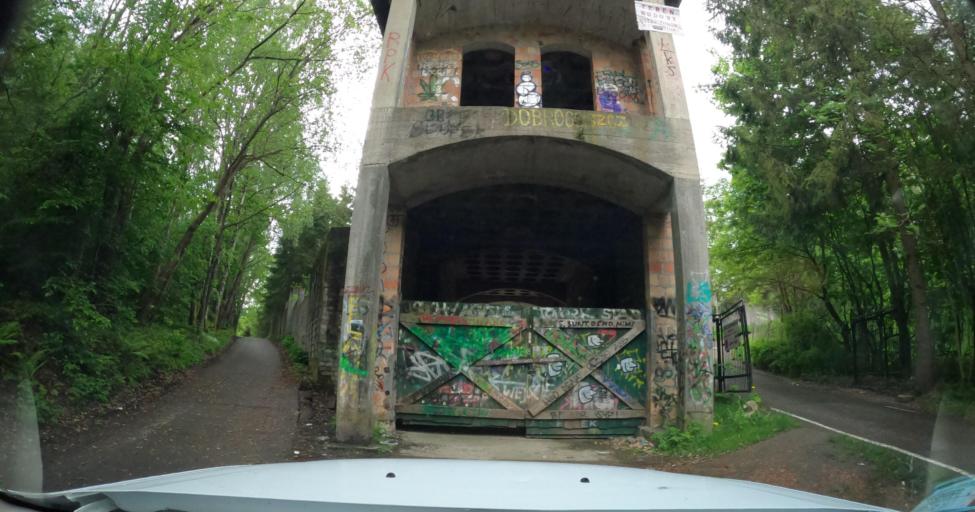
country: PL
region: Pomeranian Voivodeship
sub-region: Powiat kartuski
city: Garcz
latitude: 54.3314
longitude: 18.1404
